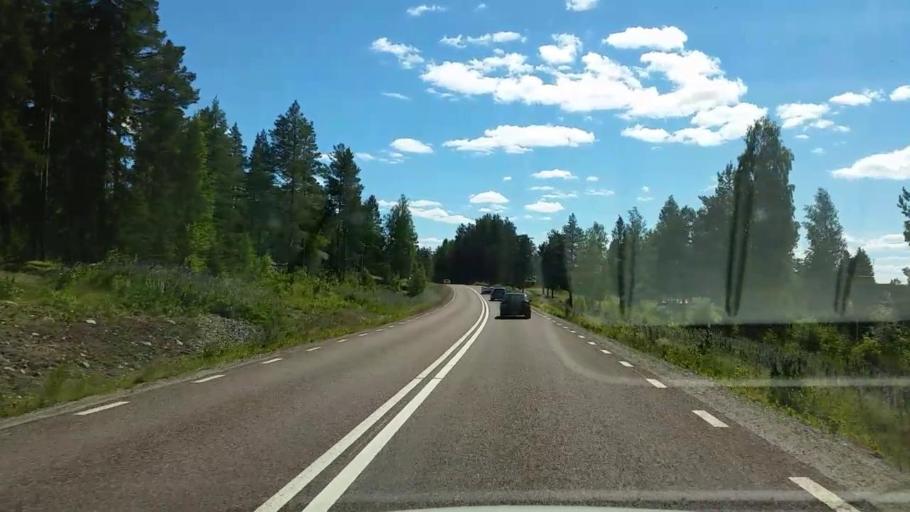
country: SE
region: Gaevleborg
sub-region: Ovanakers Kommun
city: Edsbyn
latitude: 61.2259
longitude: 15.8767
